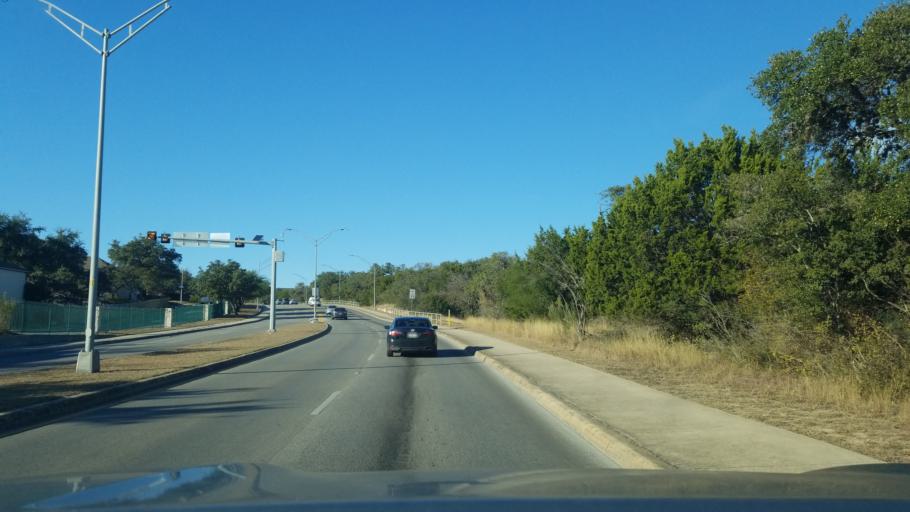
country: US
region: Texas
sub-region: Bexar County
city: Hollywood Park
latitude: 29.6318
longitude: -98.4812
